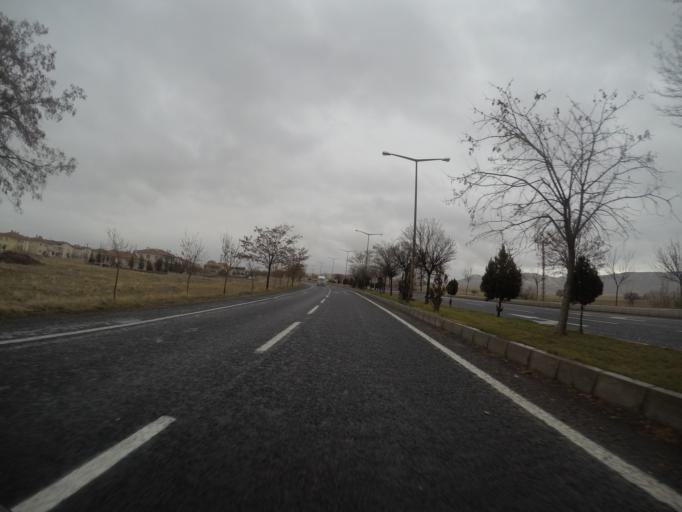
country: TR
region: Nevsehir
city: Avanos
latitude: 38.7020
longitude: 34.8586
